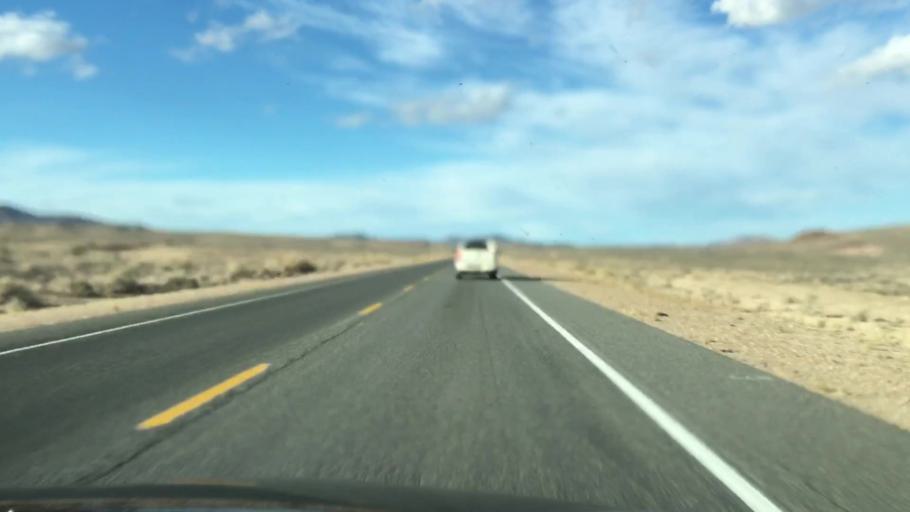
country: US
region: Nevada
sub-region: Esmeralda County
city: Goldfield
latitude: 37.5504
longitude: -117.1969
